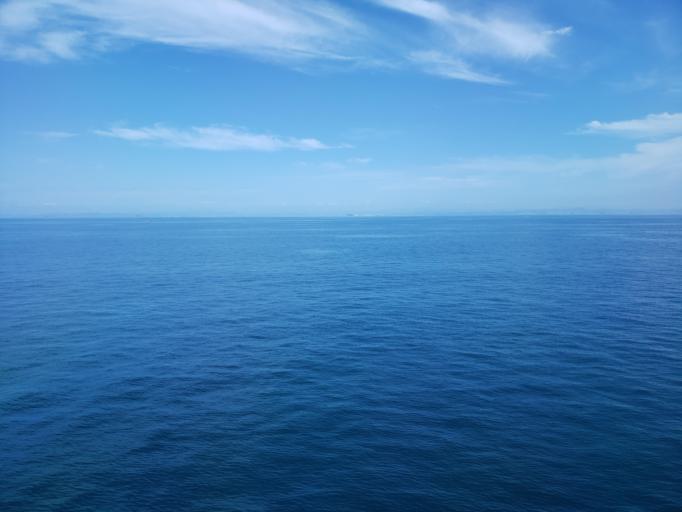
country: JP
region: Hyogo
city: Kakogawacho-honmachi
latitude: 34.5589
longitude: 134.7636
